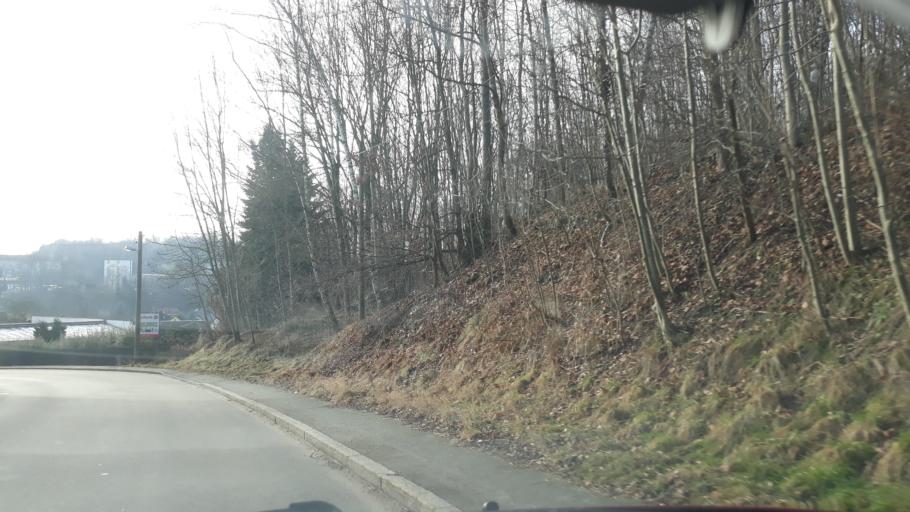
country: DE
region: Saxony
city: Wilkau-Hasslau
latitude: 50.7056
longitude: 12.5337
